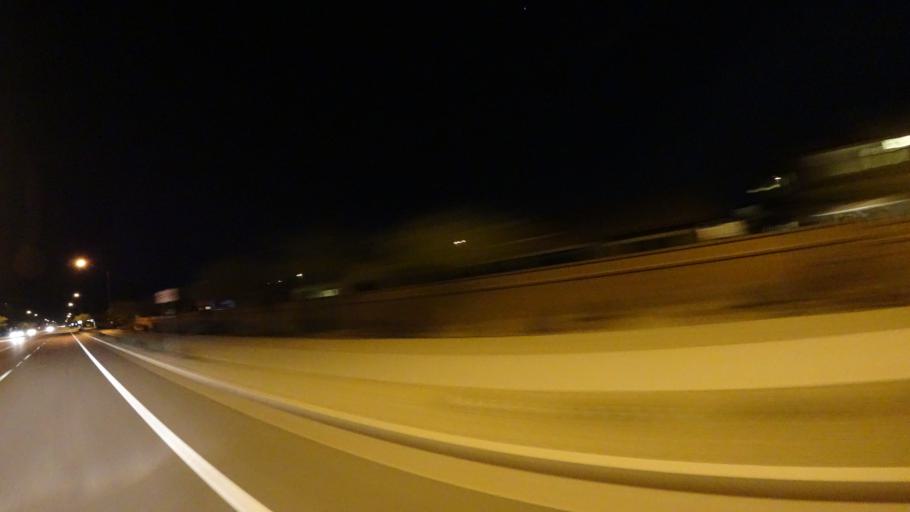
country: US
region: Arizona
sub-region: Maricopa County
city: Queen Creek
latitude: 33.2482
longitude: -111.7145
